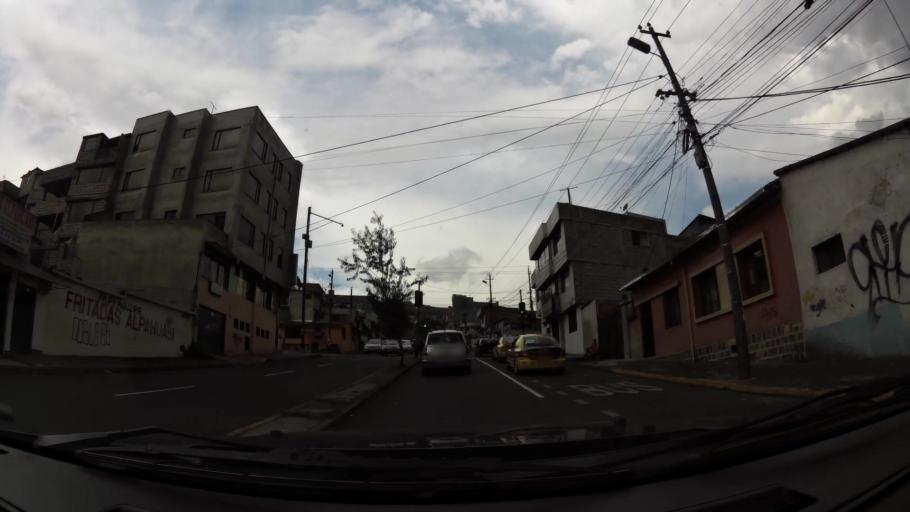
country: EC
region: Pichincha
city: Quito
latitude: -0.2444
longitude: -78.5112
